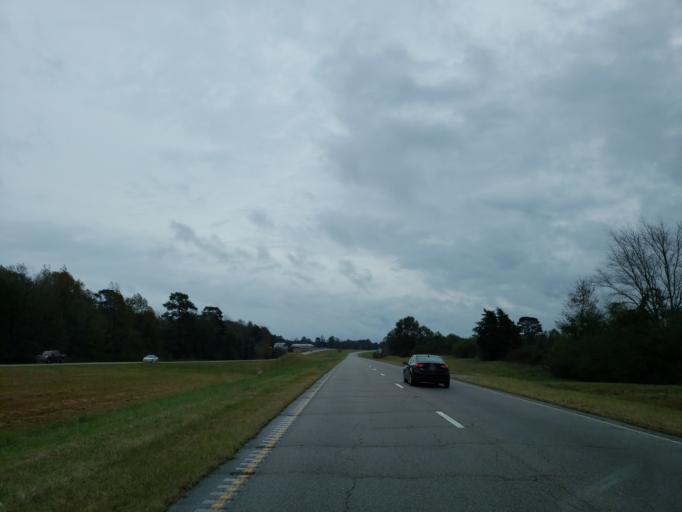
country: US
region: Mississippi
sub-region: Jones County
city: Sharon
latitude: 31.7037
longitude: -88.9172
